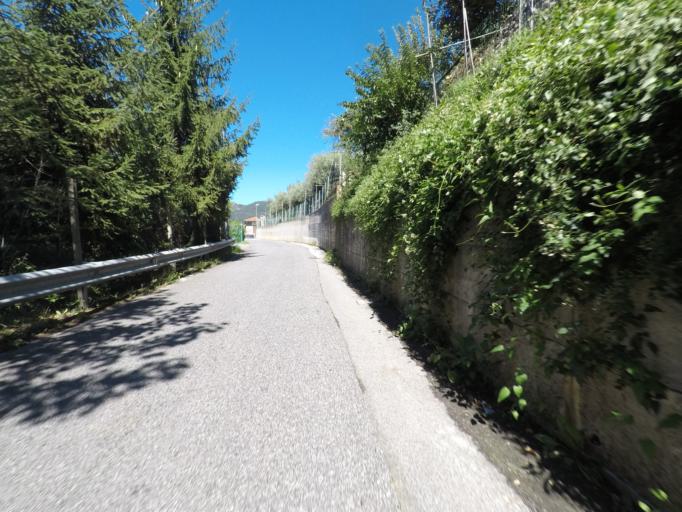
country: IT
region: Tuscany
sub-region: Provincia di Massa-Carrara
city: Montignoso
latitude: 44.0370
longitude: 10.1578
